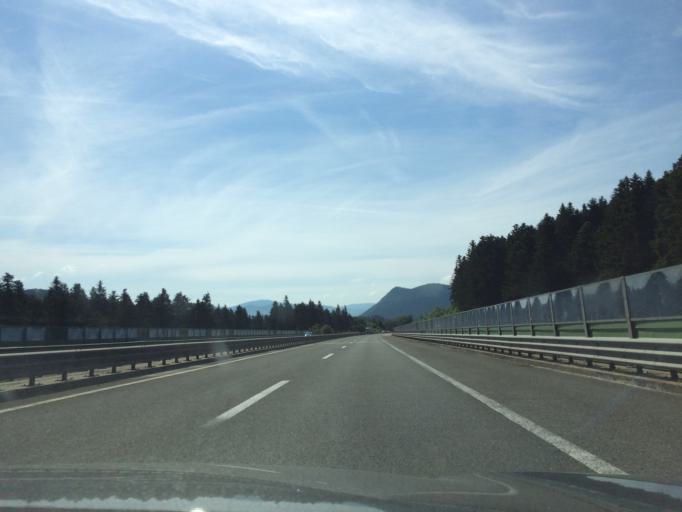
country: HR
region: Licko-Senjska
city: Otocac
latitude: 44.8470
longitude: 15.2365
